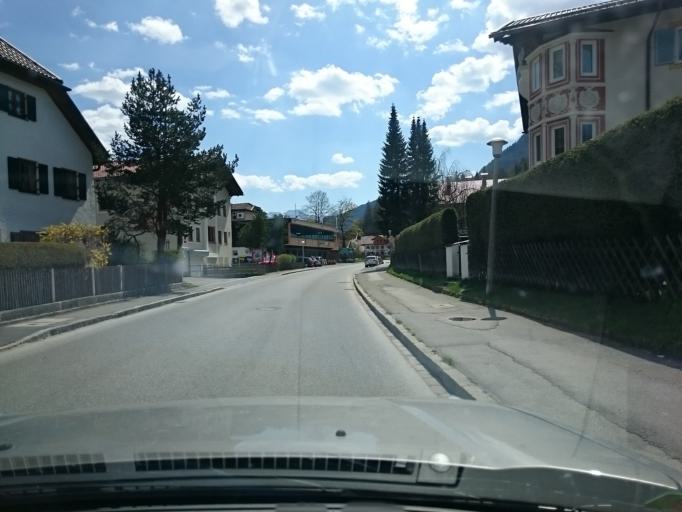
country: DE
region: Bavaria
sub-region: Upper Bavaria
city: Mittenwald
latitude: 47.4376
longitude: 11.2600
